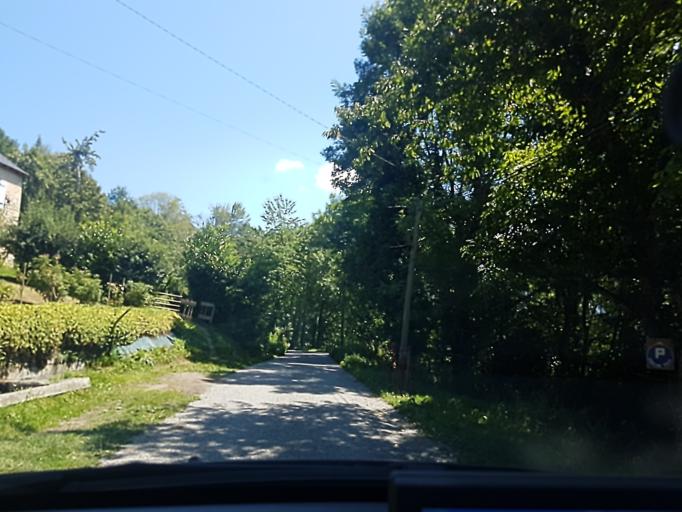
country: FR
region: Midi-Pyrenees
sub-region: Departement de l'Ariege
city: Montjoie-en-Couserans
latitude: 42.9076
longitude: 1.3390
